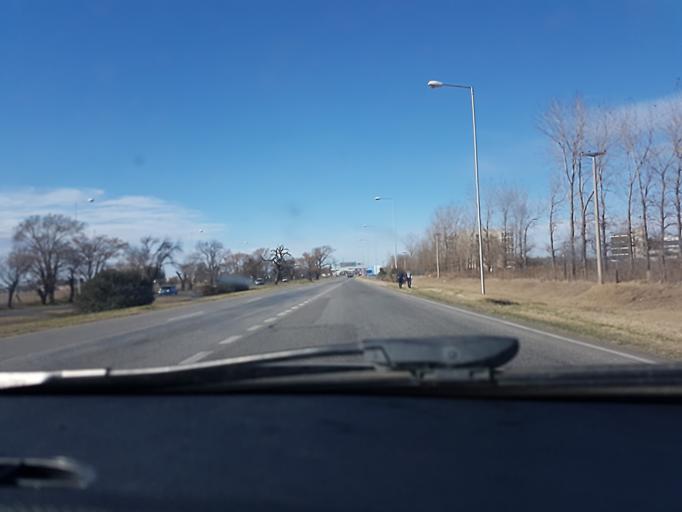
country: AR
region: Cordoba
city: Villa Allende
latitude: -31.3073
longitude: -64.2214
